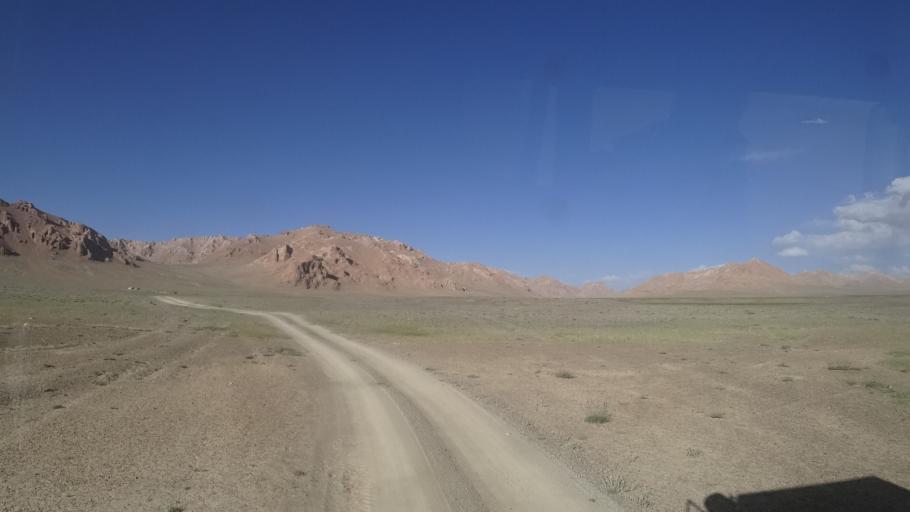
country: TJ
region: Gorno-Badakhshan
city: Murghob
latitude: 37.6561
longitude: 74.1688
